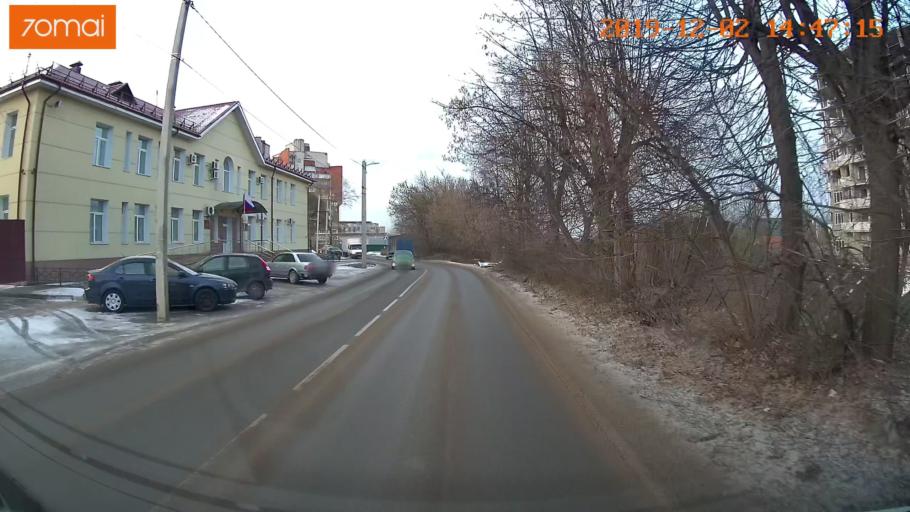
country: RU
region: Ivanovo
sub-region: Gorod Ivanovo
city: Ivanovo
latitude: 56.9881
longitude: 41.0210
